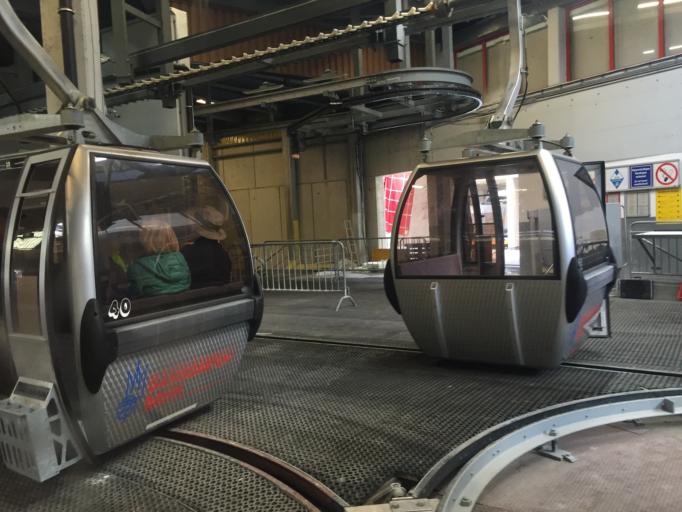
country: AT
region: Tyrol
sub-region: Politischer Bezirk Imst
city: Soelden
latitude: 46.9972
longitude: 11.1403
